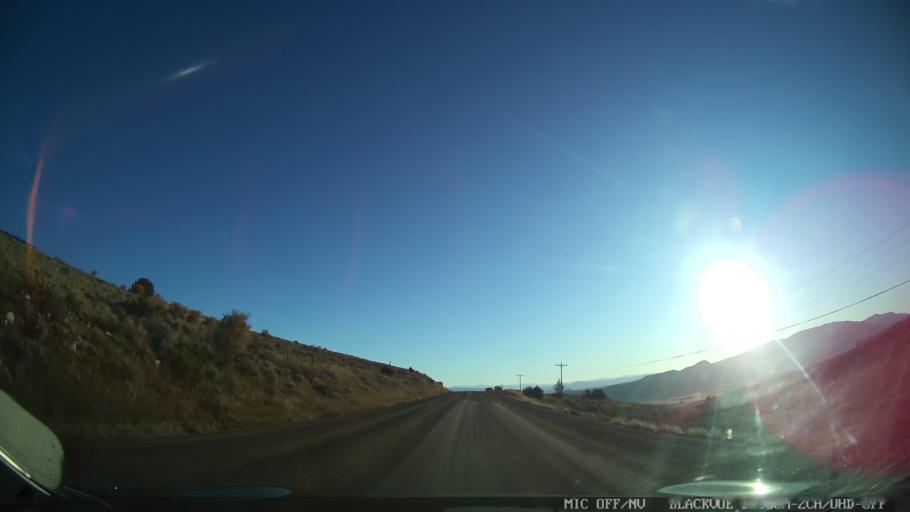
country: US
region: Colorado
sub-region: Grand County
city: Kremmling
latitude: 39.9886
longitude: -106.4278
